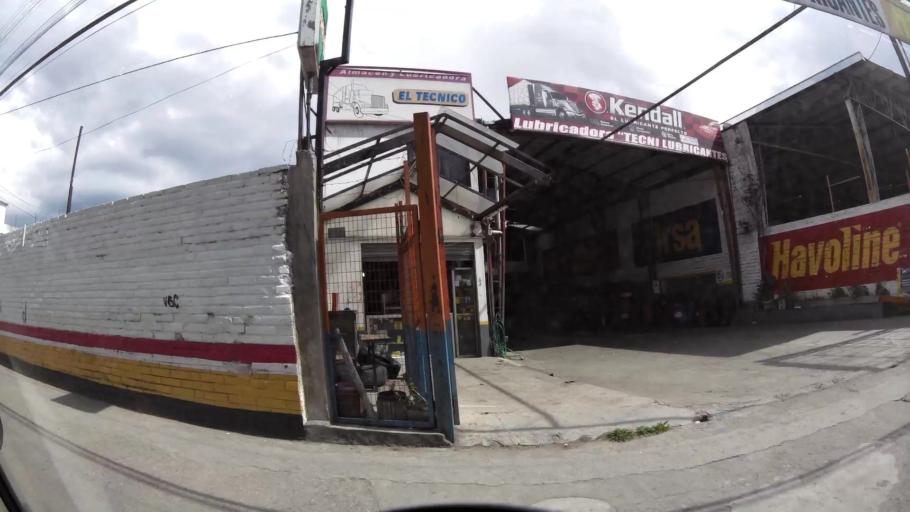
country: EC
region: Azuay
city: Cuenca
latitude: -2.8907
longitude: -78.9910
